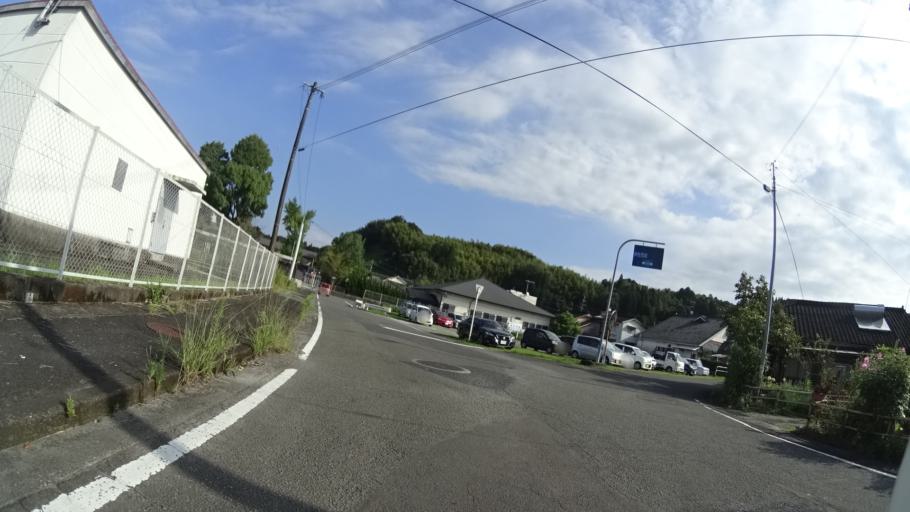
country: JP
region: Kagoshima
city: Okuchi-shinohara
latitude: 32.0103
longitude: 130.6415
